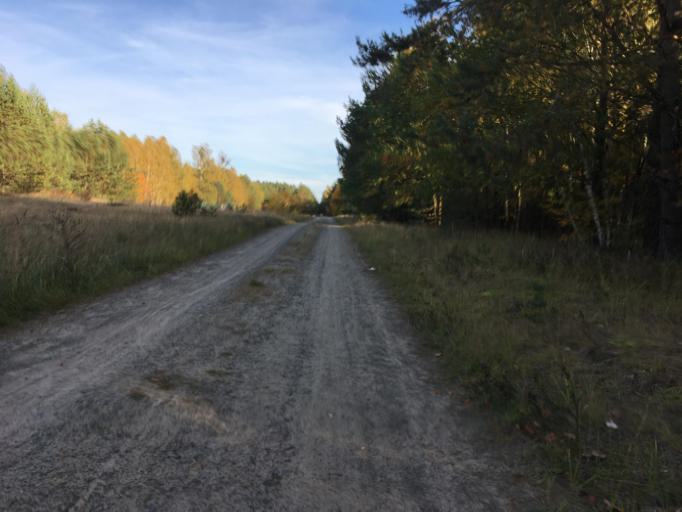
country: DE
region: Brandenburg
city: Birkenwerder
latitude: 52.7068
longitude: 13.3420
